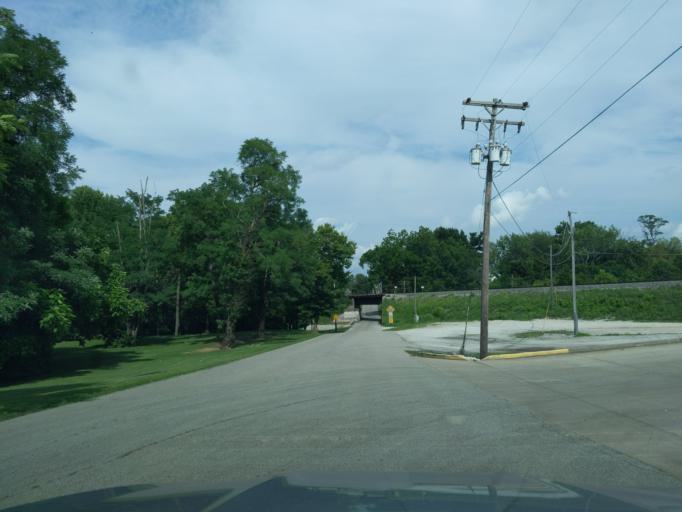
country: US
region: Indiana
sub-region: Ripley County
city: Osgood
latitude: 39.1328
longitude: -85.2902
